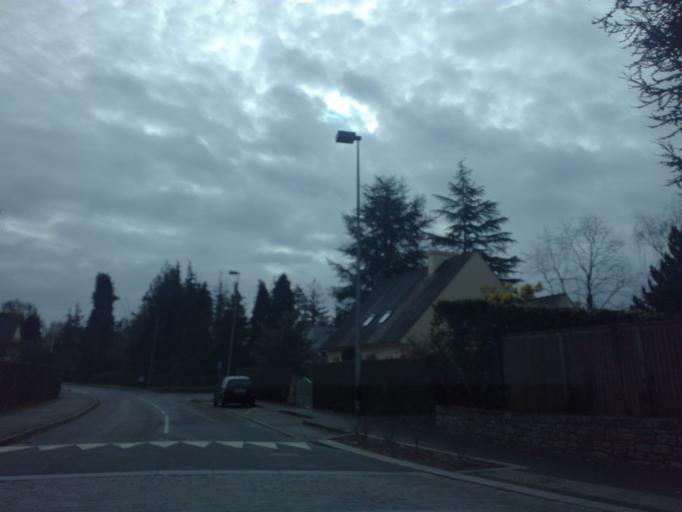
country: FR
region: Brittany
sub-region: Departement d'Ille-et-Vilaine
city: Saint-Gregoire
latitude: 48.1529
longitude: -1.6822
